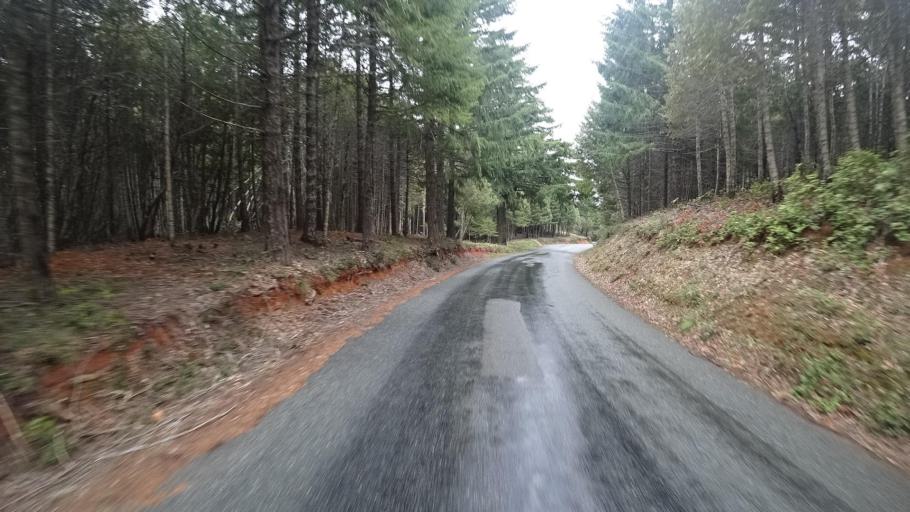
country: US
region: California
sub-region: Humboldt County
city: Willow Creek
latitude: 41.2020
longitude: -123.7964
